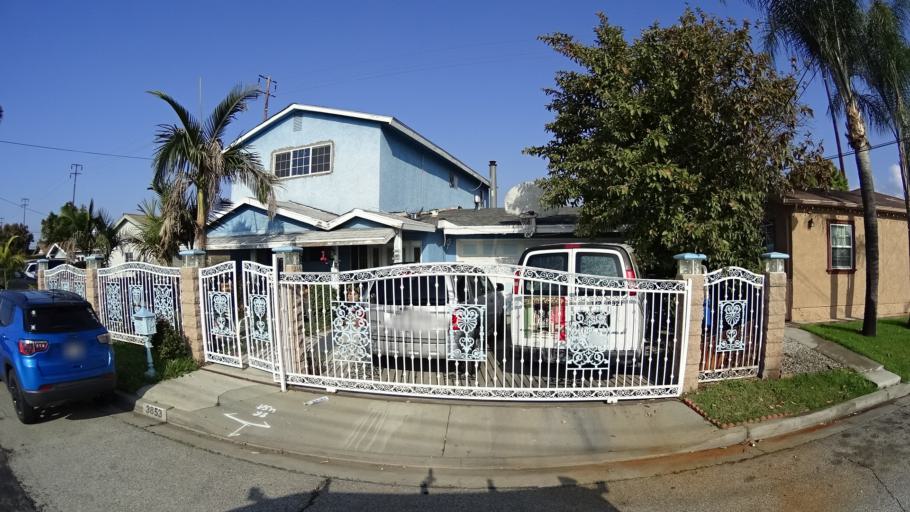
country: US
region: California
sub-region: Los Angeles County
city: Baldwin Park
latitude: 34.0827
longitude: -117.9542
